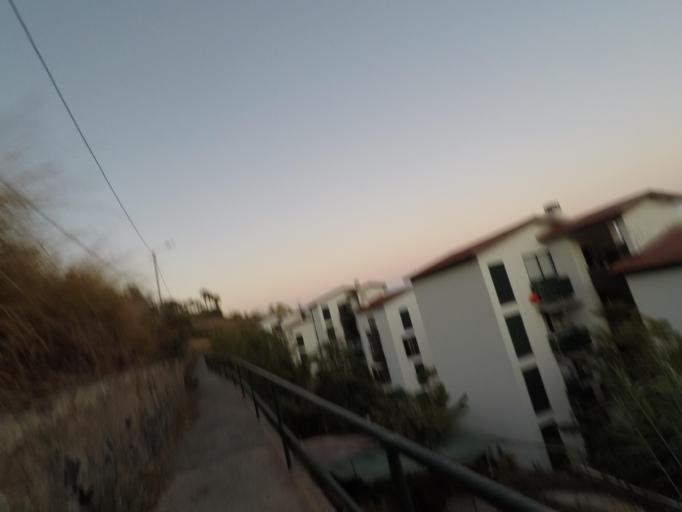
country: PT
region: Madeira
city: Camara de Lobos
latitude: 32.6403
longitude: -16.9371
